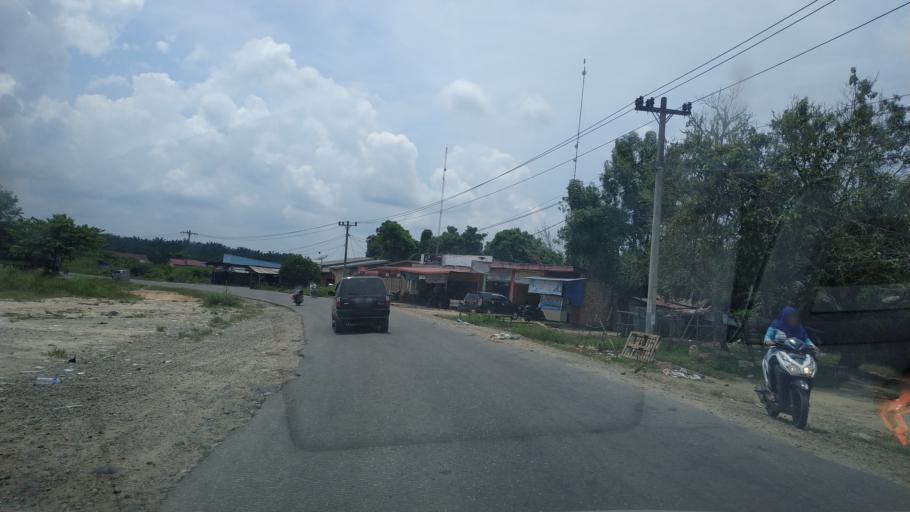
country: ID
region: North Sumatra
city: Langgapayung
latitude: 1.7170
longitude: 99.9230
